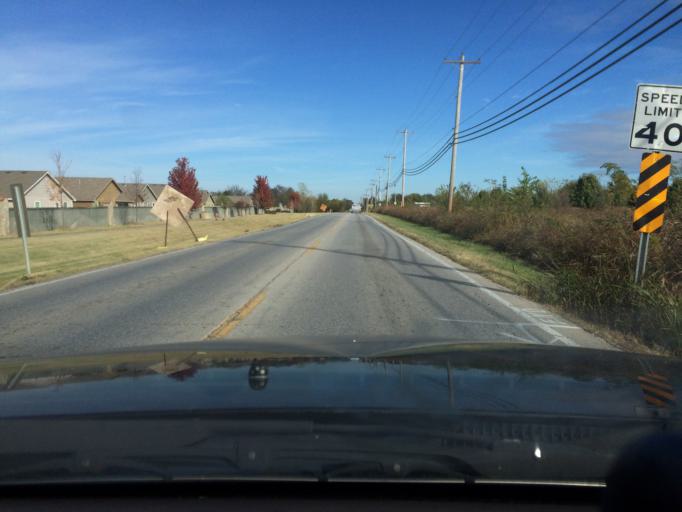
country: US
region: Oklahoma
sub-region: Tulsa County
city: Broken Arrow
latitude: 36.0806
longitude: -95.7617
